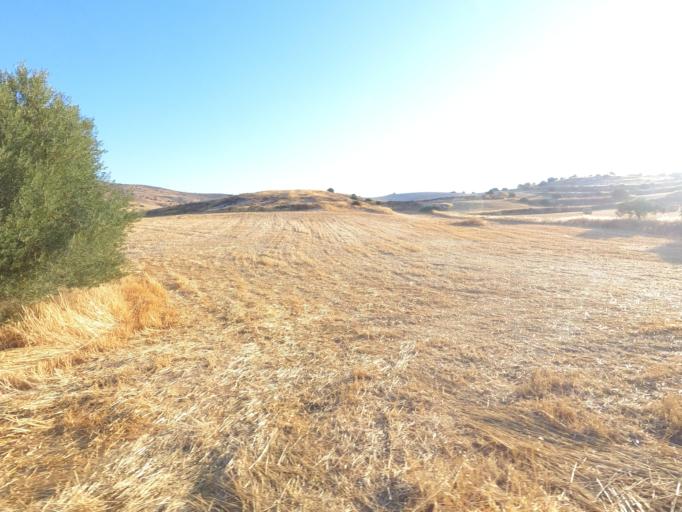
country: CY
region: Larnaka
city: Troulloi
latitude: 35.0289
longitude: 33.6485
